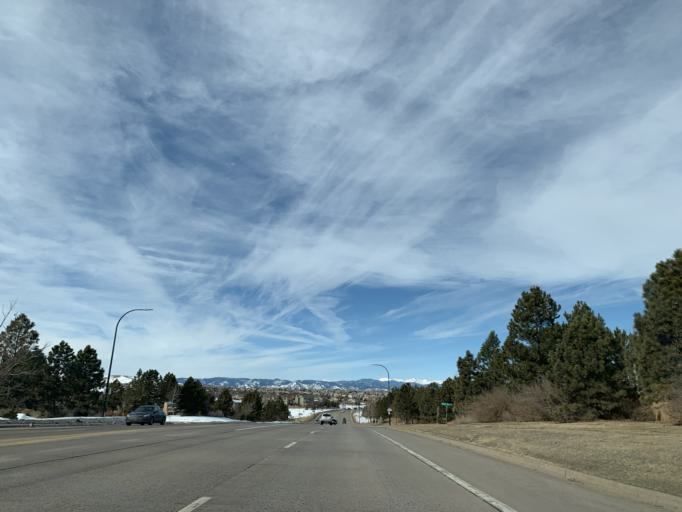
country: US
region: Colorado
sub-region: Douglas County
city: Carriage Club
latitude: 39.5217
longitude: -104.9240
